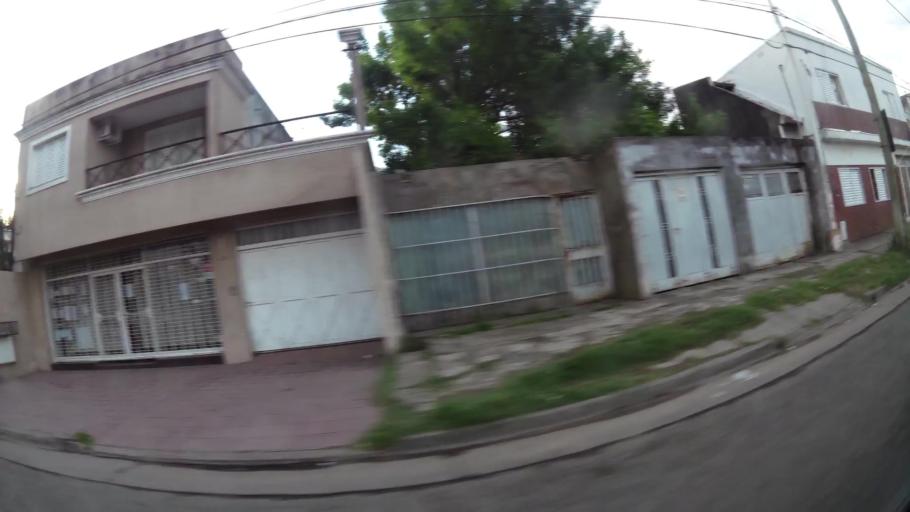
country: AR
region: Buenos Aires
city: San Nicolas de los Arroyos
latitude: -33.3242
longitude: -60.2310
